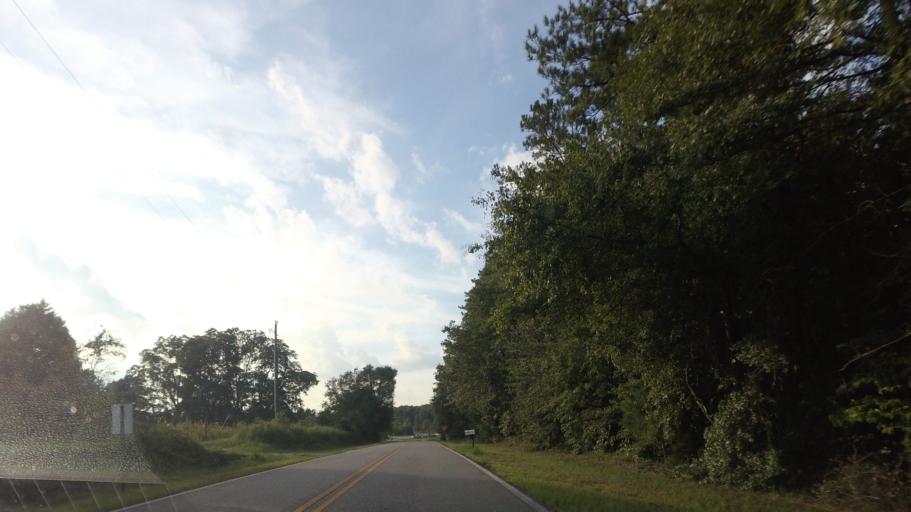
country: US
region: Georgia
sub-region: Wilkinson County
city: Gordon
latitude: 32.8461
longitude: -83.4199
